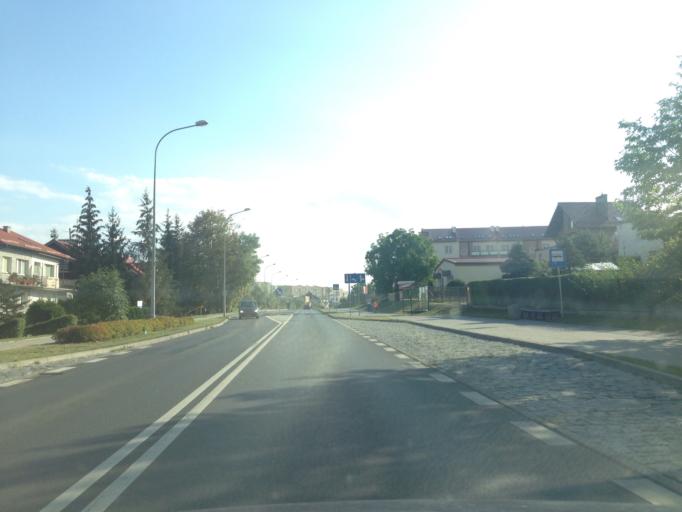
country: PL
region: Warmian-Masurian Voivodeship
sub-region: Powiat ilawski
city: Ilawa
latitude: 53.6085
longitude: 19.5693
